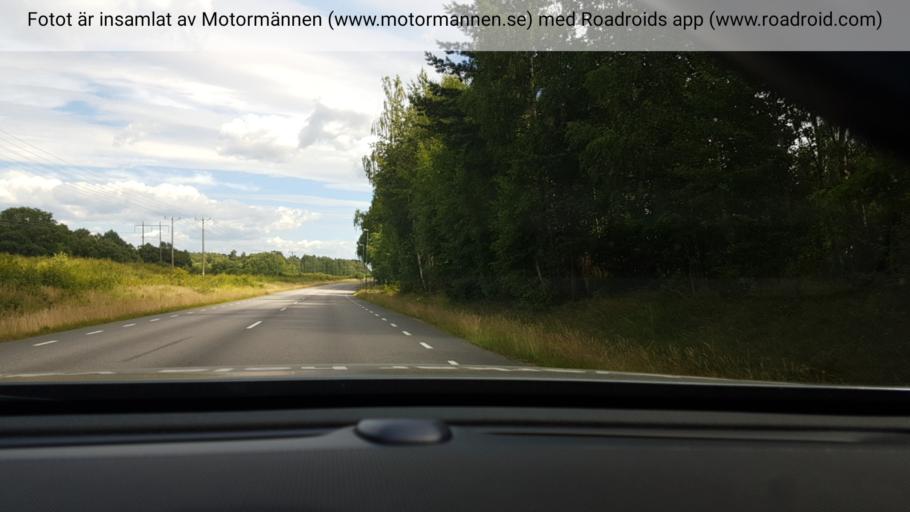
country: SE
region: Skane
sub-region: Hassleholms Kommun
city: Hassleholm
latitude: 56.1756
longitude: 13.7916
